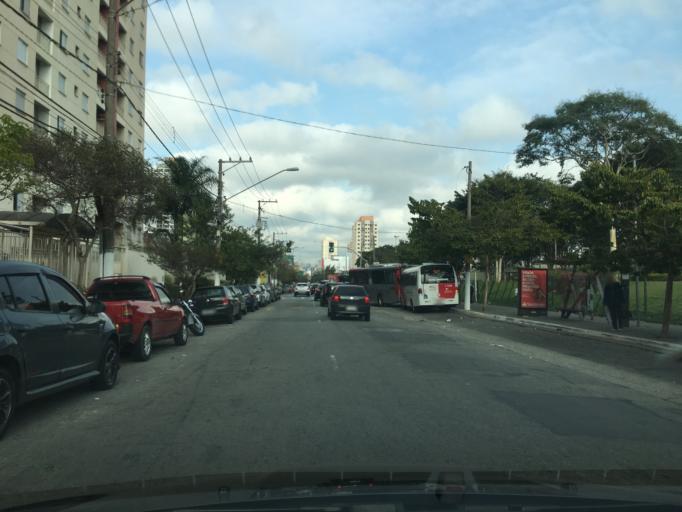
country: BR
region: Sao Paulo
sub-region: Sao Paulo
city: Sao Paulo
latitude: -23.5463
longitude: -46.6053
